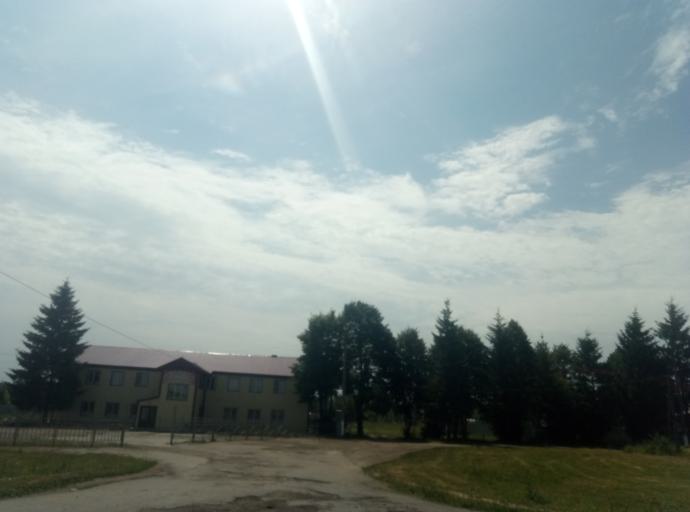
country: RU
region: Tula
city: Dubovka
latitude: 53.9041
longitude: 38.0270
